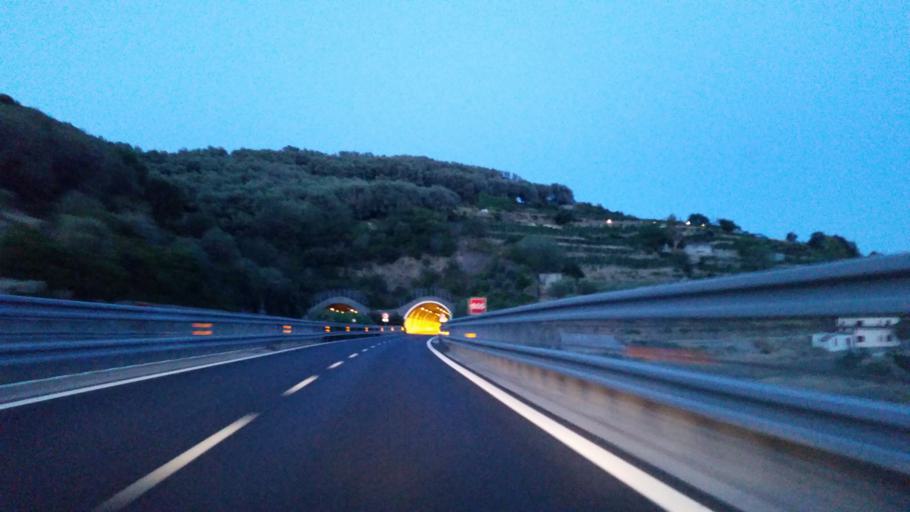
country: IT
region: Liguria
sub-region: Provincia di Imperia
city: San Lorenzo al Mare
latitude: 43.8630
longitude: 7.9580
